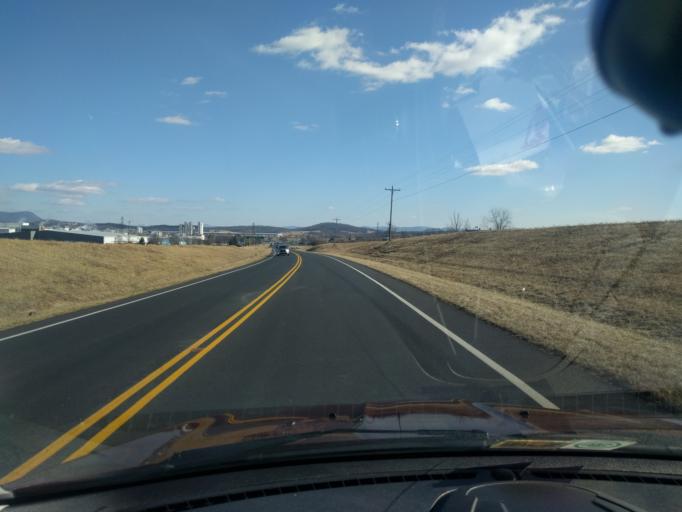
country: US
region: Virginia
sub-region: Rockingham County
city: Bridgewater
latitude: 38.3671
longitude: -78.9448
